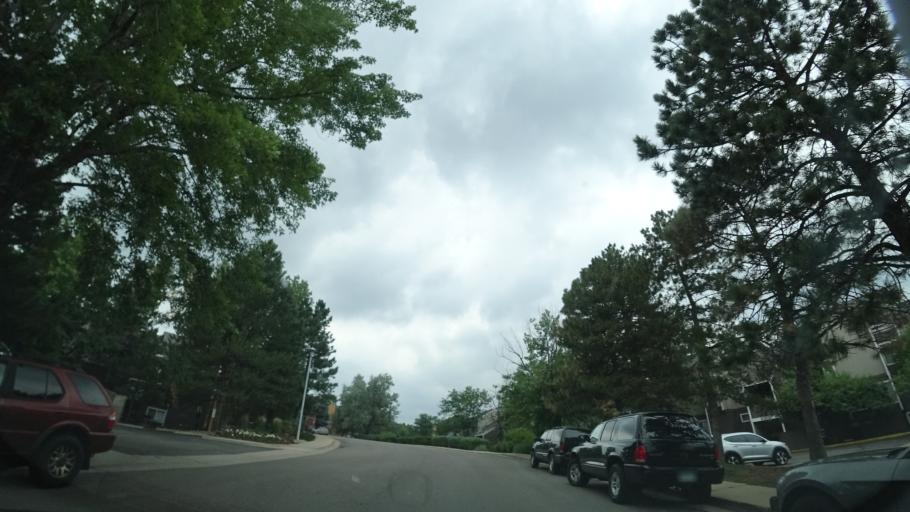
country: US
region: Colorado
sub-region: Jefferson County
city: West Pleasant View
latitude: 39.7133
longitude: -105.1442
